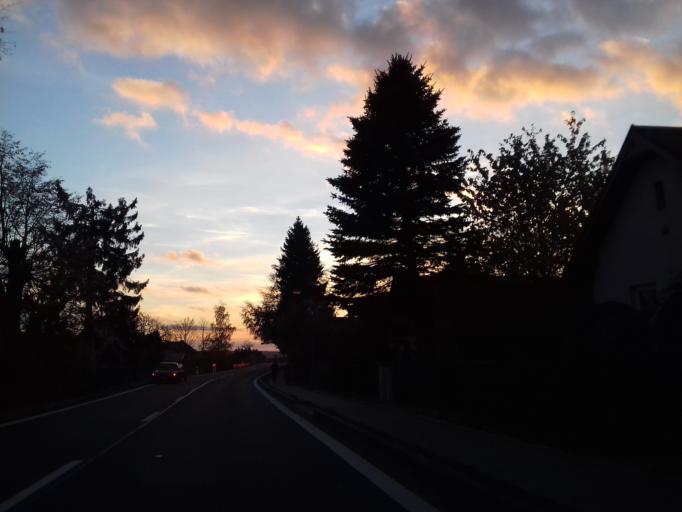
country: CZ
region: Vysocina
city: Krizova
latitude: 49.7068
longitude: 15.8412
